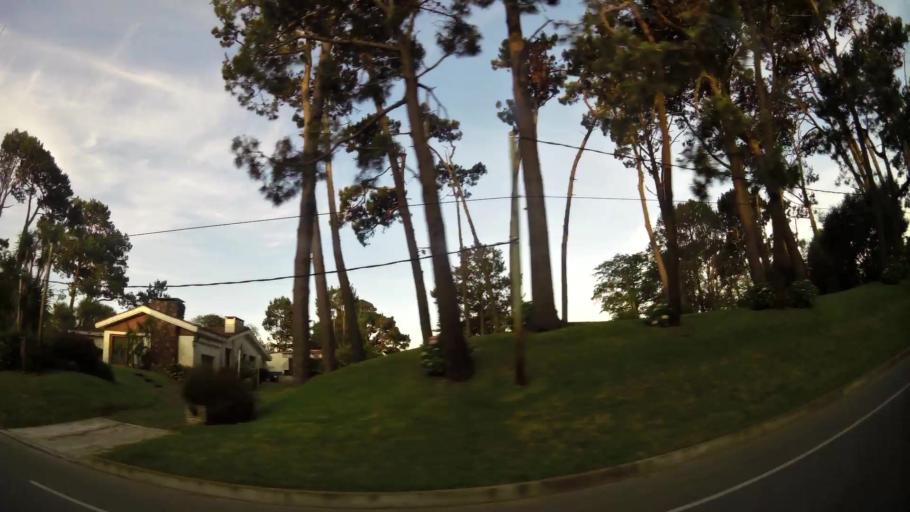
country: UY
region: Maldonado
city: Maldonado
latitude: -34.9191
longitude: -54.9482
